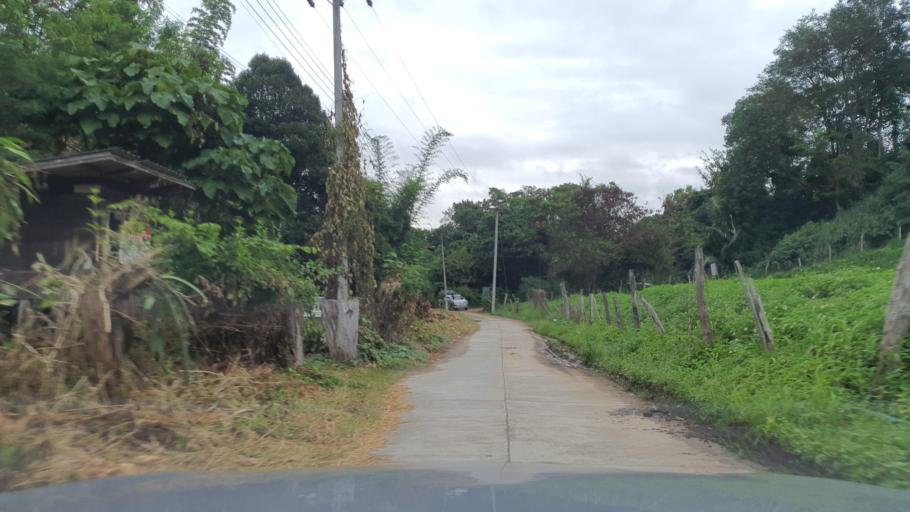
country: TH
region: Chiang Mai
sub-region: Amphoe Chiang Dao
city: Chiang Dao
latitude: 19.3283
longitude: 98.9393
